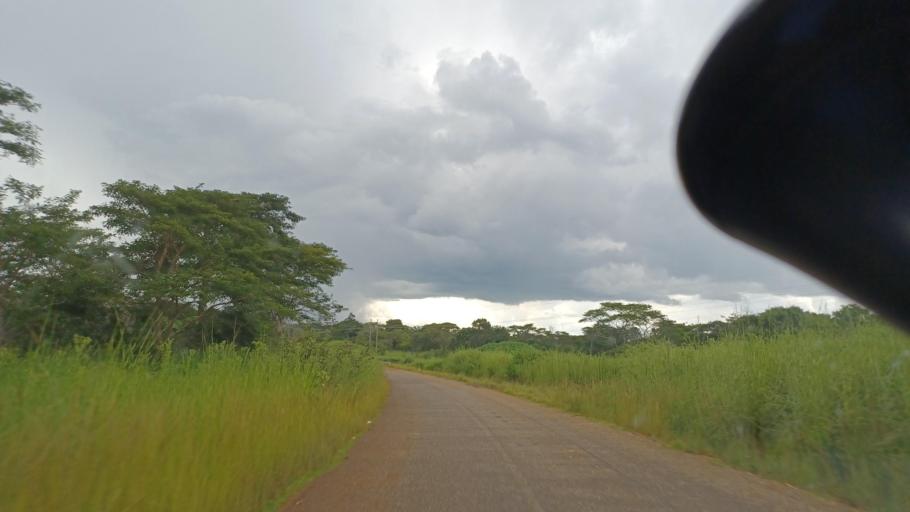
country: ZM
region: North-Western
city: Kasempa
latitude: -13.0116
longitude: 26.0042
